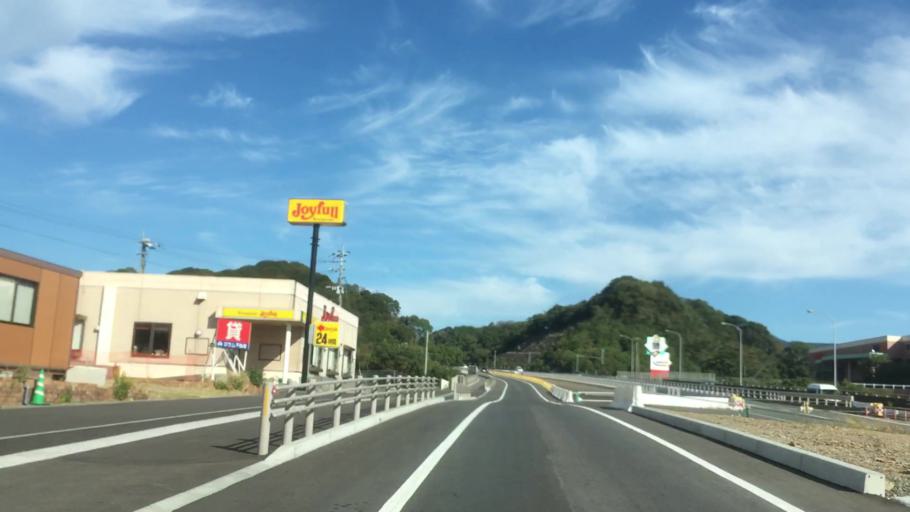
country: JP
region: Nagasaki
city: Sasebo
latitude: 33.1180
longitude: 129.7926
